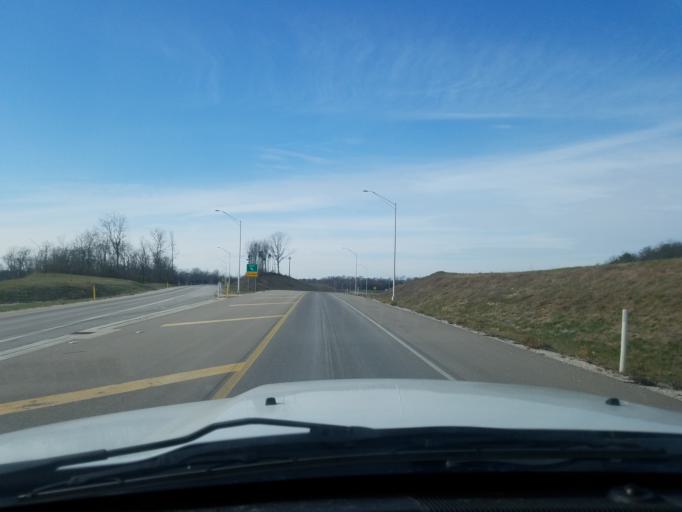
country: US
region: Indiana
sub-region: Monroe County
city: Bloomington
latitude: 39.1082
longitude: -86.5554
